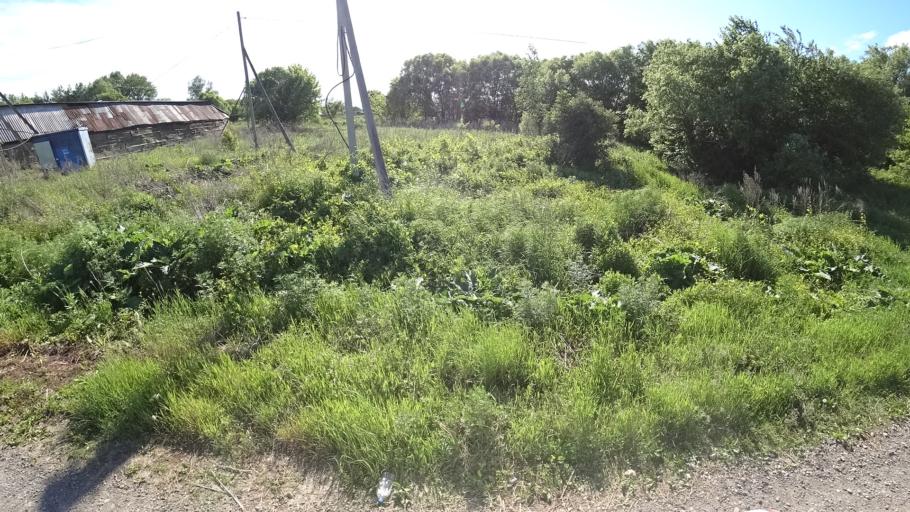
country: RU
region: Khabarovsk Krai
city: Khor
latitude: 47.8875
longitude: 134.9986
